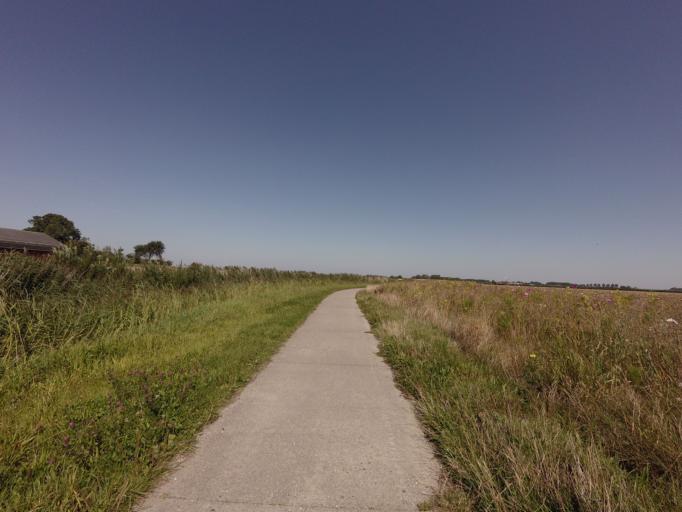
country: NL
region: Friesland
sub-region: Gemeente Dongeradeel
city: Anjum
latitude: 53.3908
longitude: 6.0660
